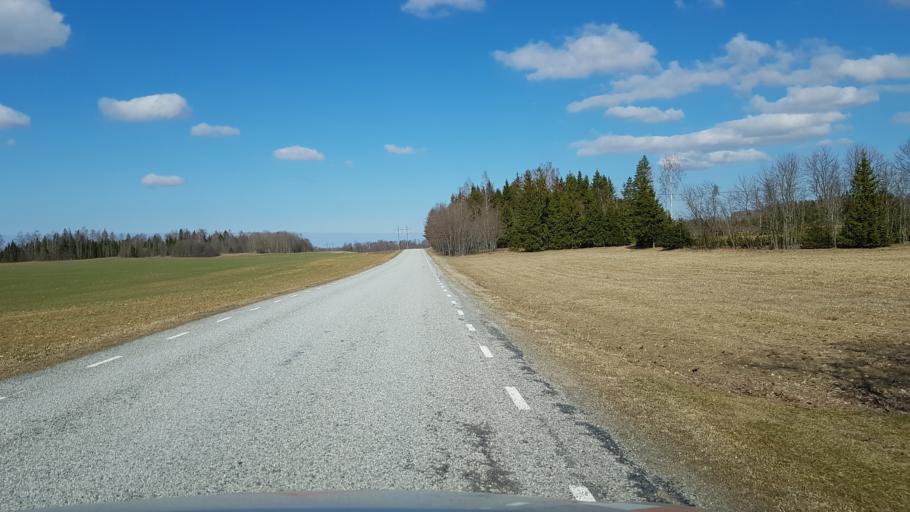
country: EE
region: Laeaene-Virumaa
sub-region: Kadrina vald
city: Kadrina
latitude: 59.2975
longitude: 26.2146
